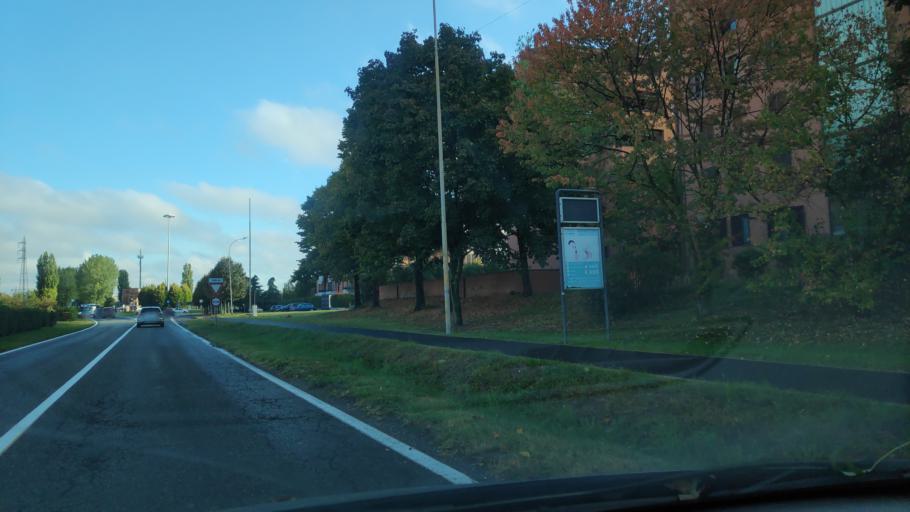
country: IT
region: Lombardy
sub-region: Citta metropolitana di Milano
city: Opera
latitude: 45.3807
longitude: 9.2130
